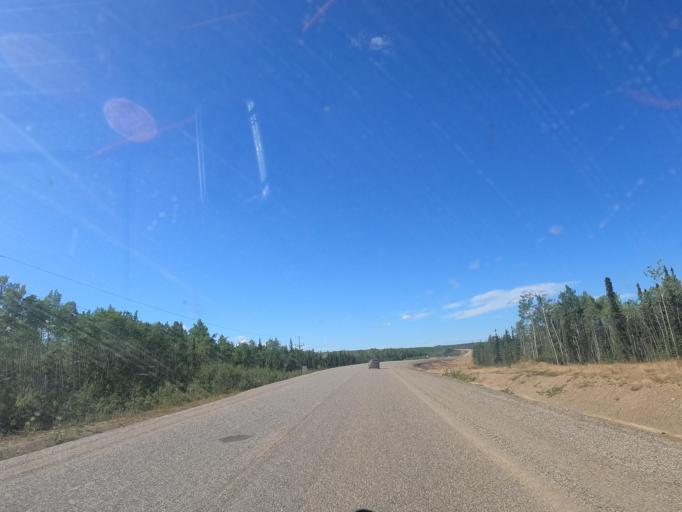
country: CA
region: Yukon
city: Dawson City
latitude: 63.8739
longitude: -138.1345
